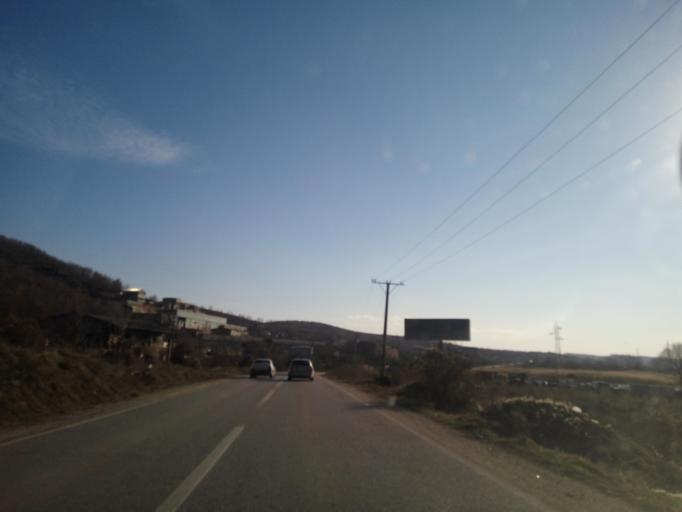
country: XK
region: Pristina
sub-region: Komuna e Prishtines
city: Pristina
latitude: 42.6078
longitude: 21.2205
